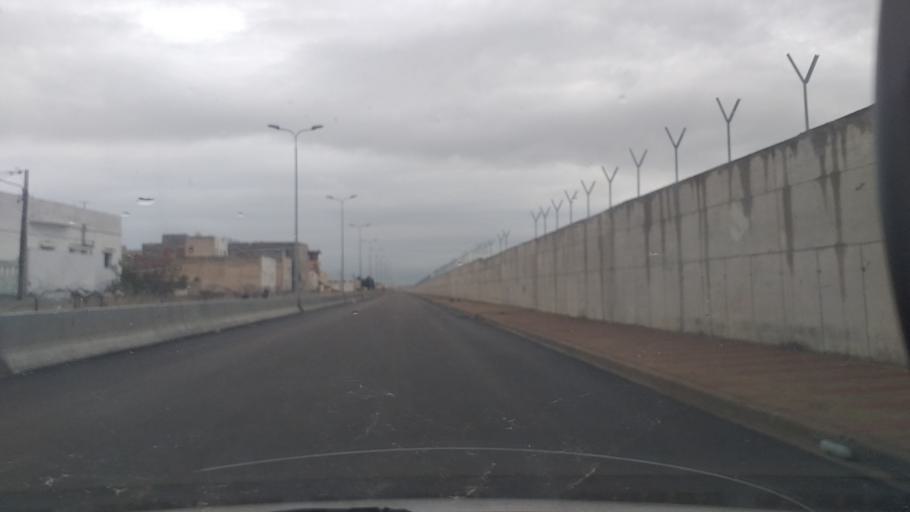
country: TN
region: Ariana
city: Ariana
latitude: 36.8631
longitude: 10.2206
